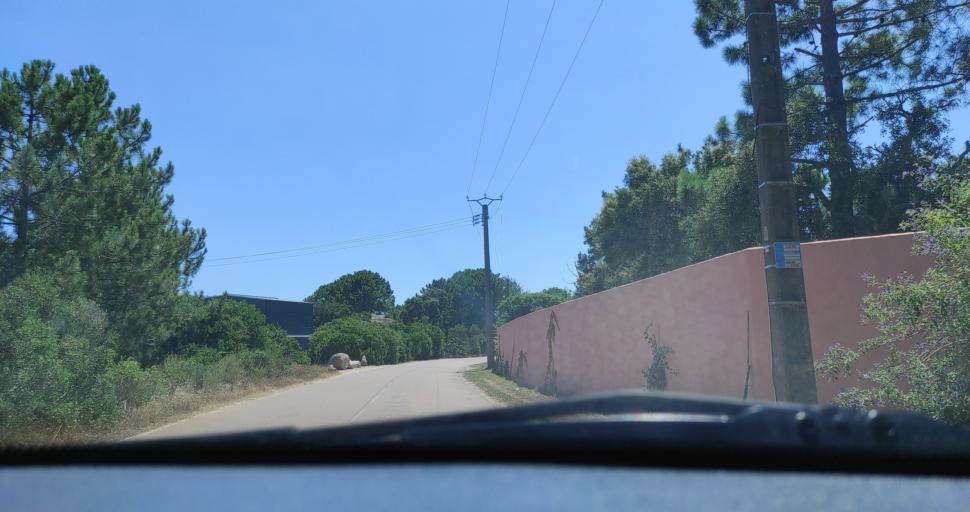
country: FR
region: Corsica
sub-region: Departement de la Corse-du-Sud
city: Porto-Vecchio
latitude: 41.6266
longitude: 9.3362
